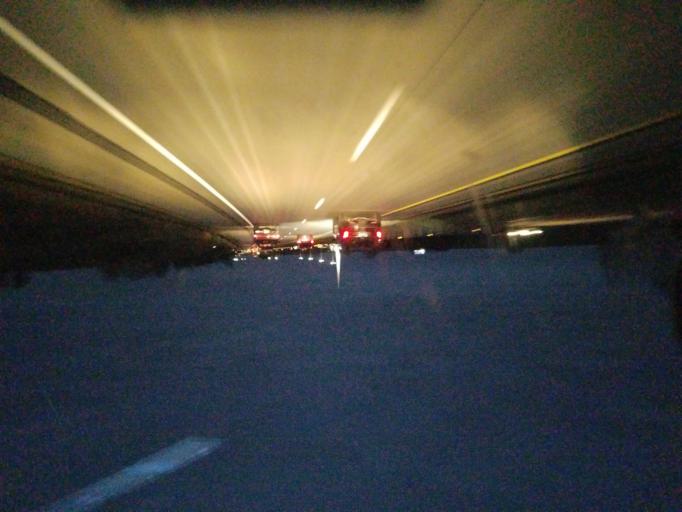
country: US
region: Iowa
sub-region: Guthrie County
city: Guthrie Center
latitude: 41.4965
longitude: -94.5786
